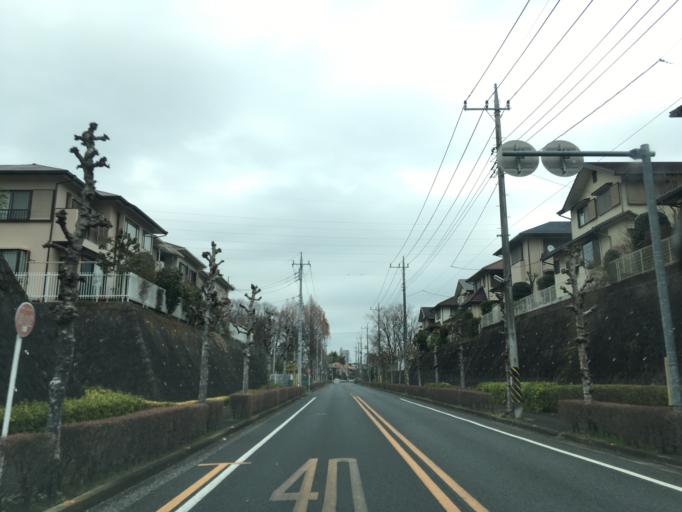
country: JP
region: Tokyo
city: Higashimurayama-shi
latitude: 35.7734
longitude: 139.4586
